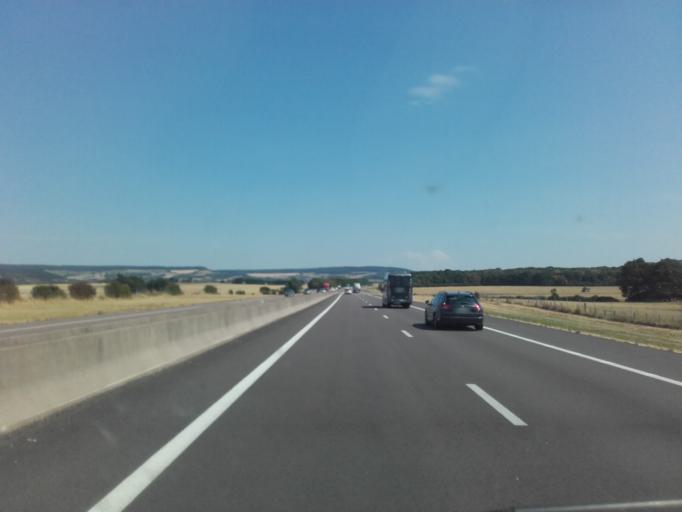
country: FR
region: Bourgogne
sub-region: Departement de la Cote-d'Or
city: Vitteaux
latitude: 47.3557
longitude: 4.4366
